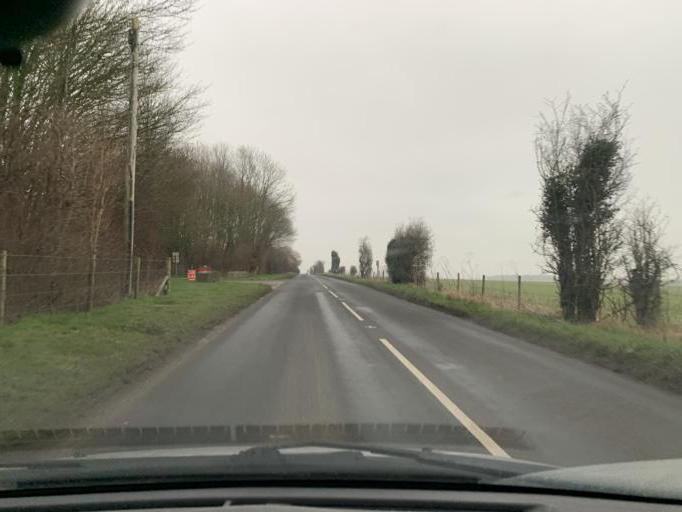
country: GB
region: England
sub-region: Wiltshire
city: Shrewton
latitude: 51.2013
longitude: -1.8697
